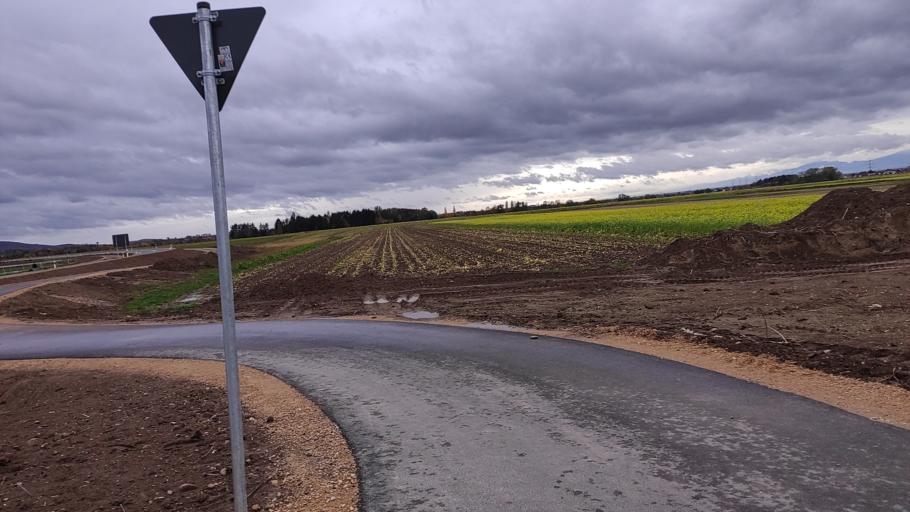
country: DE
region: Baden-Wuerttemberg
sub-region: Freiburg Region
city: Bad Krozingen
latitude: 47.8899
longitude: 7.7167
